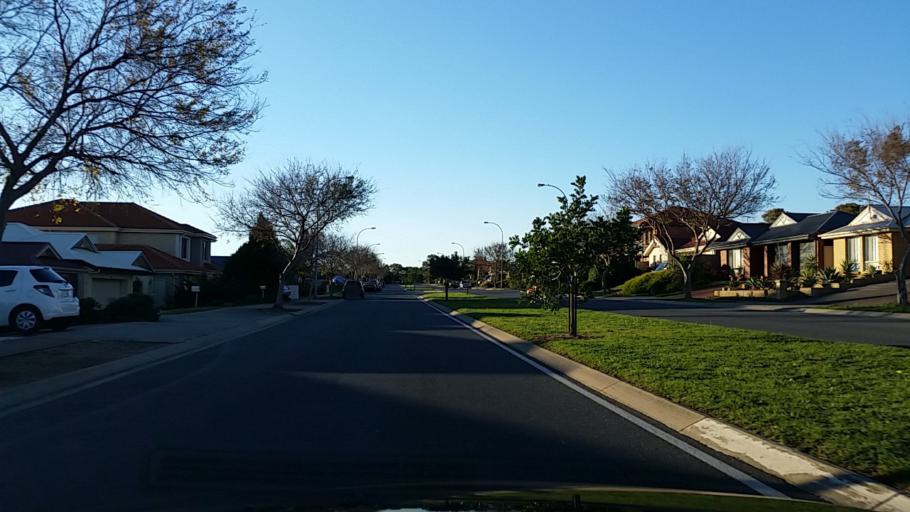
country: AU
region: South Australia
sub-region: Onkaparinga
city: Moana
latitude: -35.2045
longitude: 138.4831
